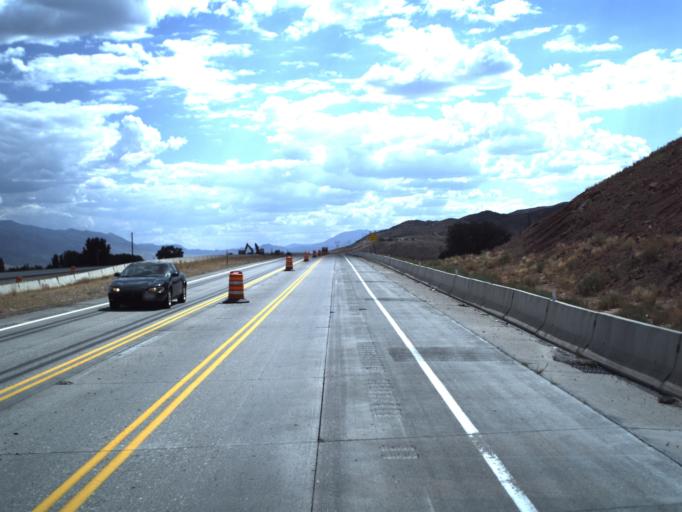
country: US
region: Utah
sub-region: Sevier County
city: Richfield
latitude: 38.7749
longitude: -112.0980
